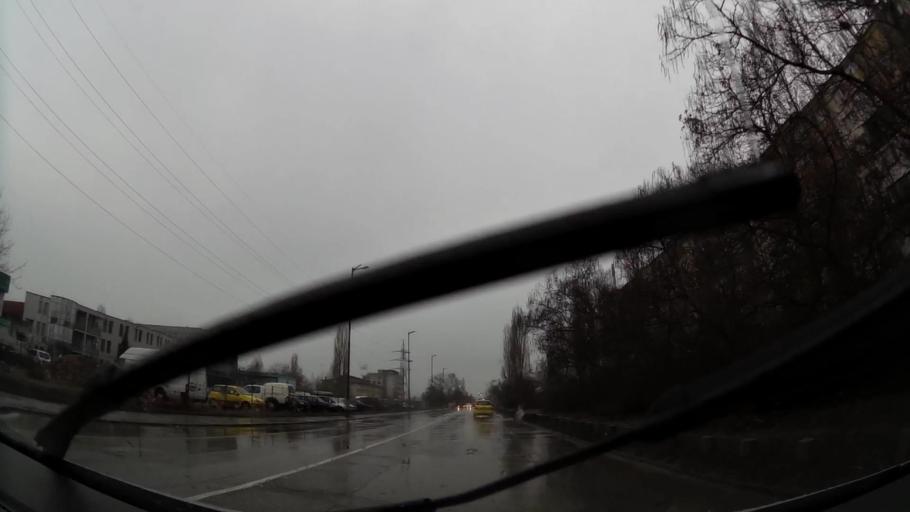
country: BG
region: Sofia-Capital
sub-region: Stolichna Obshtina
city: Sofia
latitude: 42.6692
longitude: 23.4001
